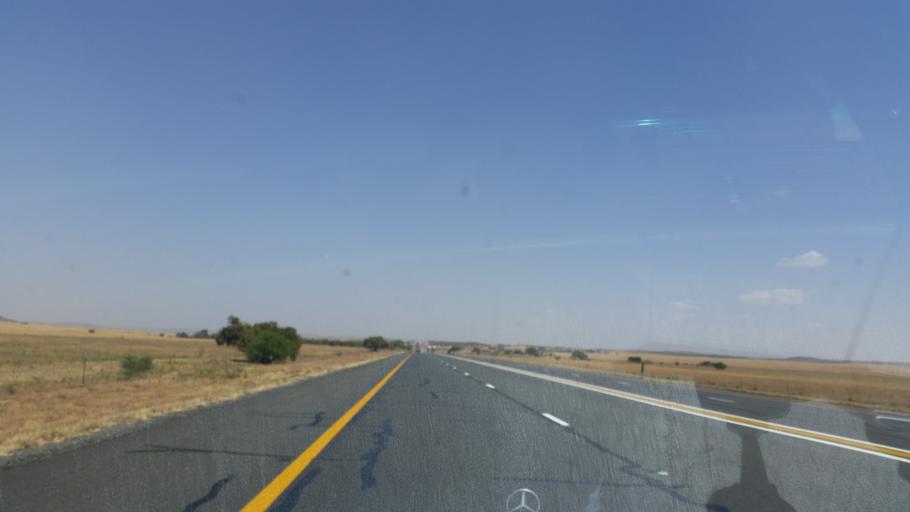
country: ZA
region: Orange Free State
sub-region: Lejweleputswa District Municipality
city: Brandfort
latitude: -28.8899
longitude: 26.4838
